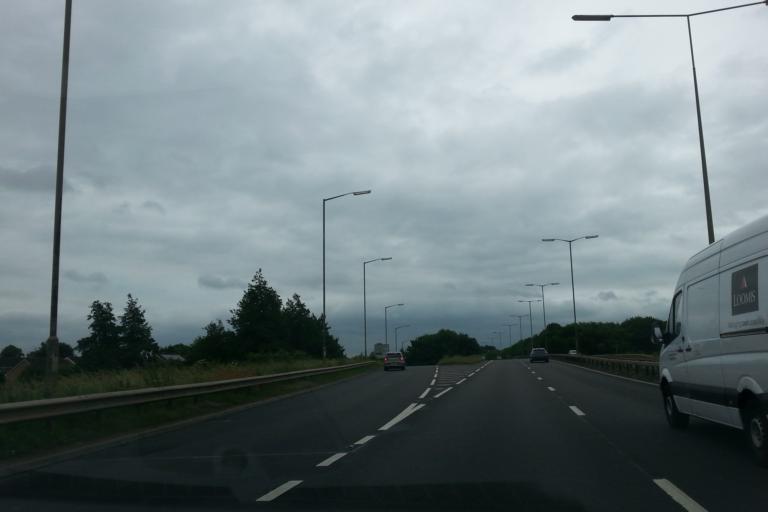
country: GB
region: England
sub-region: Peterborough
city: Peterborough
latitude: 52.5590
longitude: -0.2781
